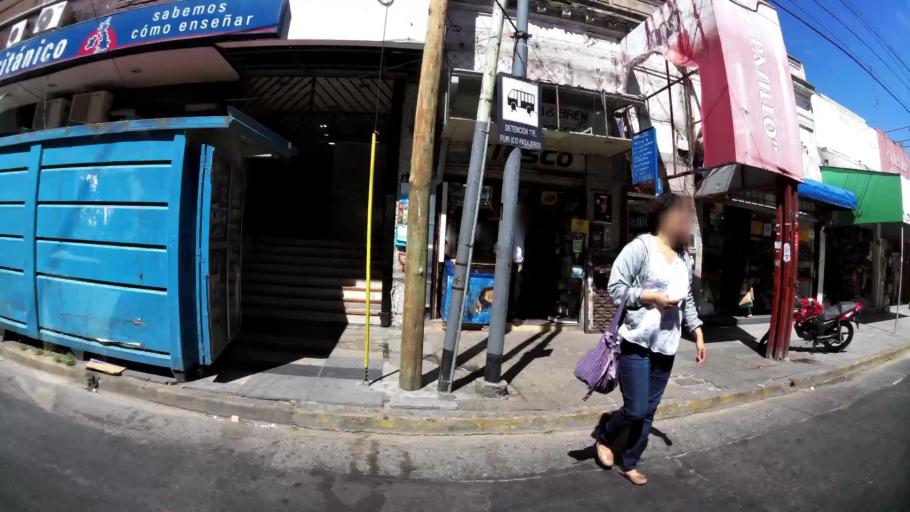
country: AR
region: Buenos Aires
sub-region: Partido de General San Martin
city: General San Martin
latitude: -34.5770
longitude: -58.5388
